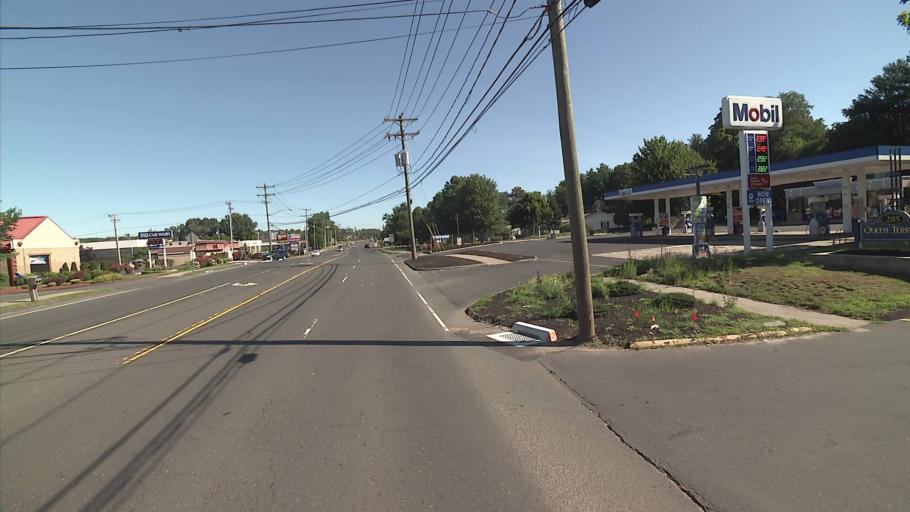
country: US
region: Connecticut
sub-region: Hartford County
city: Plainville
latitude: 41.6246
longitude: -72.8731
